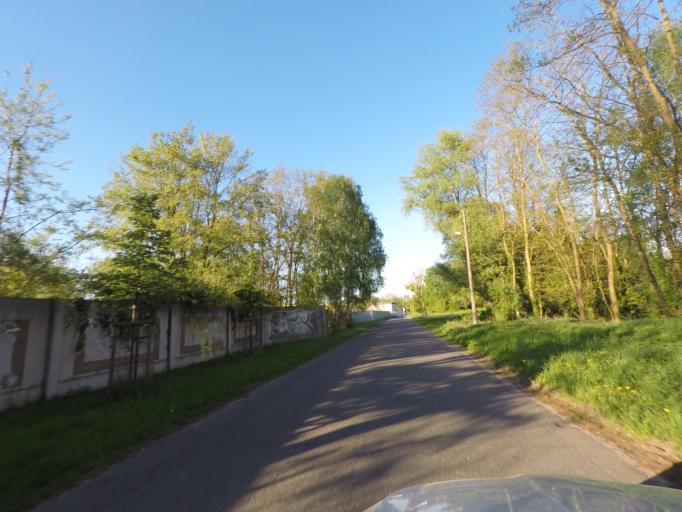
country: DE
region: Brandenburg
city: Oderberg
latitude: 52.8405
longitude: 14.0135
